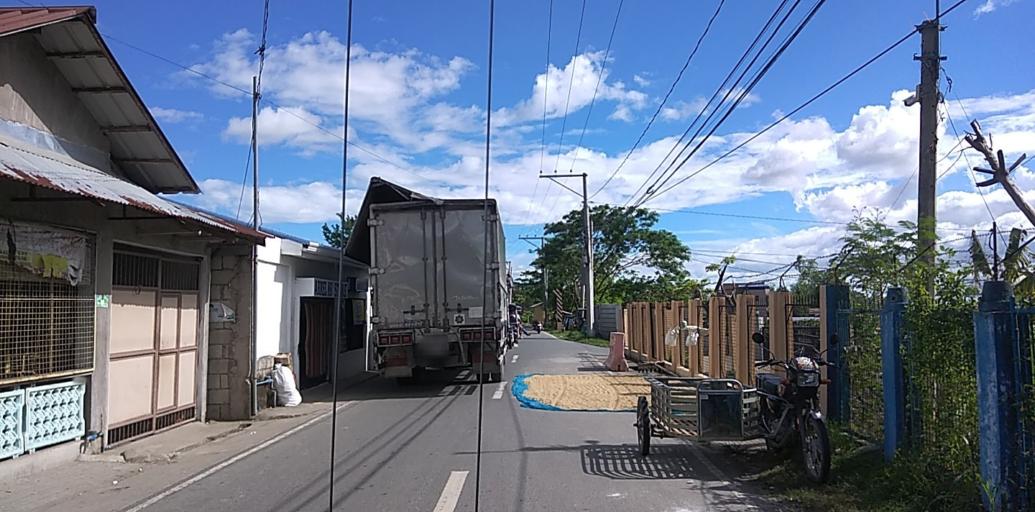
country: PH
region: Central Luzon
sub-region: Province of Pampanga
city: Arayat
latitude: 15.1351
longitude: 120.7870
